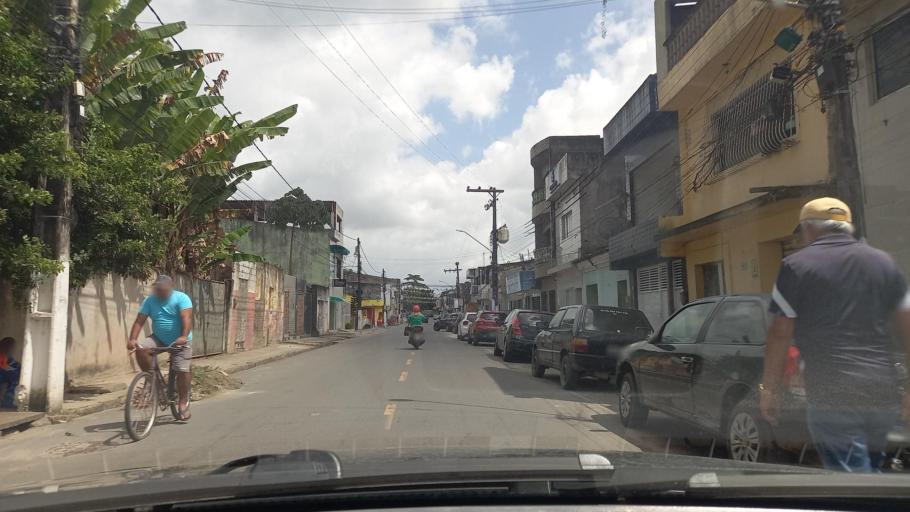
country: BR
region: Pernambuco
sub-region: Goiana
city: Goiana
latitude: -7.5573
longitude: -35.0034
